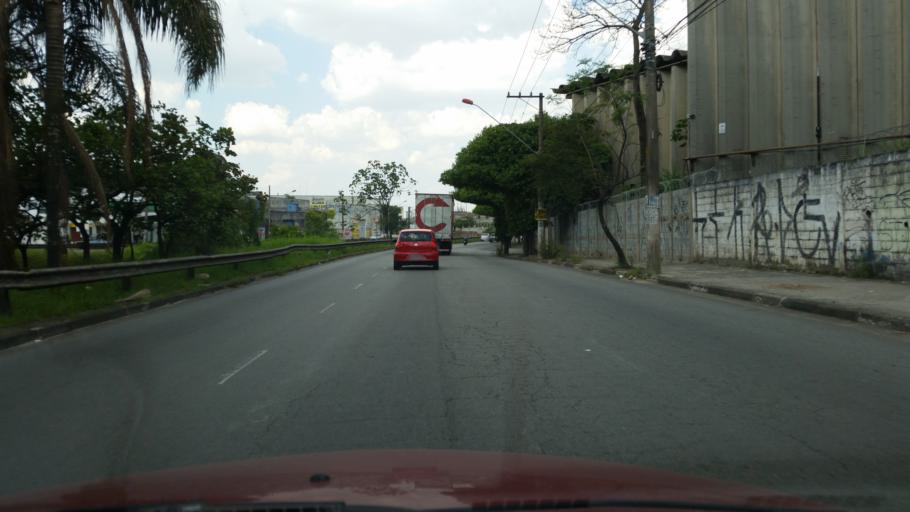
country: BR
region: Sao Paulo
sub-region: Diadema
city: Diadema
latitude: -23.6797
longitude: -46.5949
